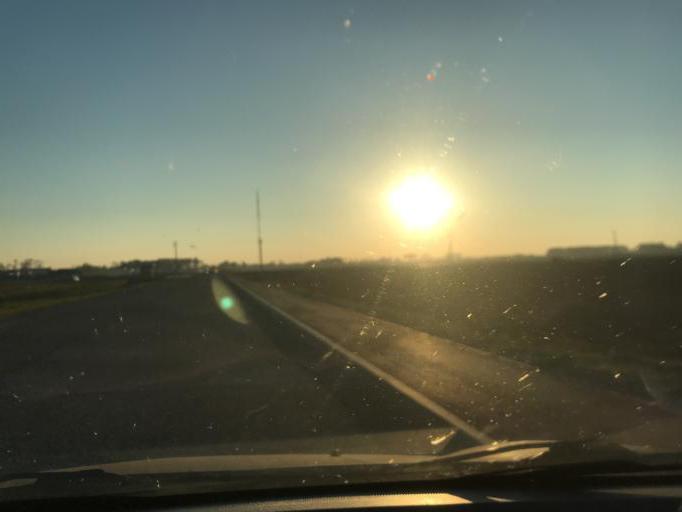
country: BY
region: Gomel
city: Brahin
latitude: 51.8062
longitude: 30.2774
